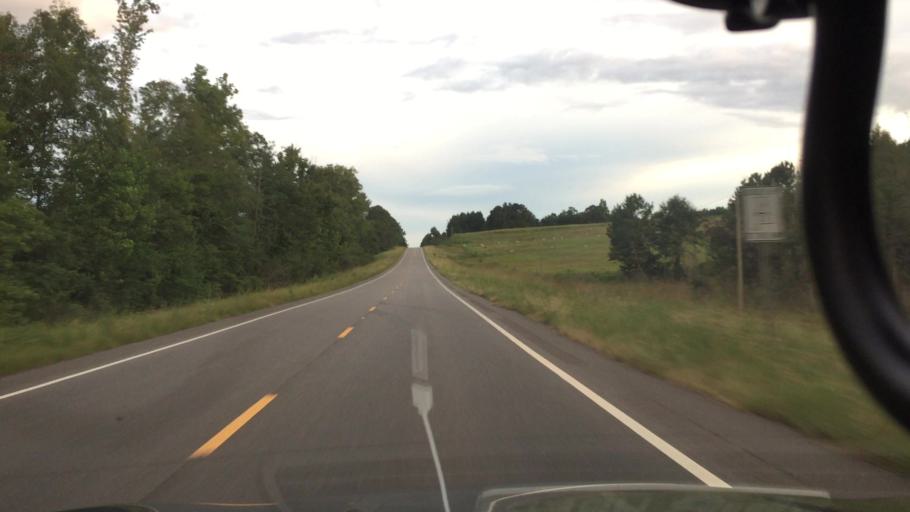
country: US
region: Alabama
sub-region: Pike County
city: Brundidge
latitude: 31.6185
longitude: -85.9461
